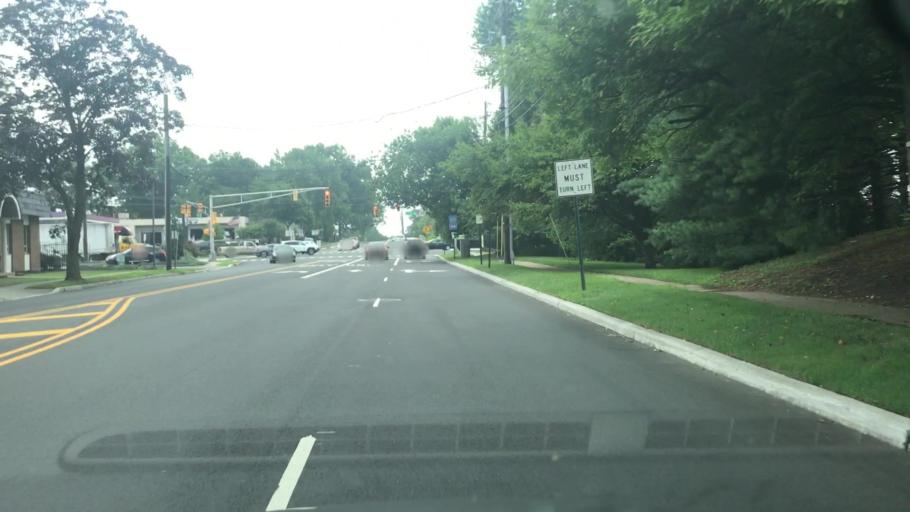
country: US
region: New Jersey
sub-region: Union County
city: Clark
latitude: 40.6351
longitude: -74.3039
